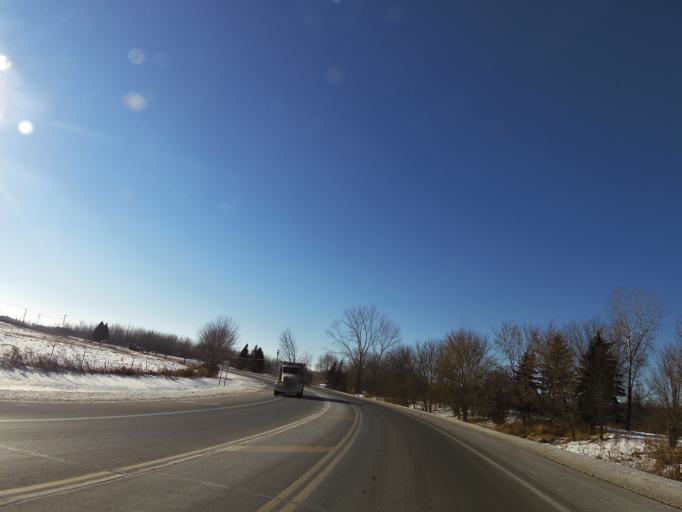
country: US
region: Minnesota
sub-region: Carver County
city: Chaska
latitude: 44.8075
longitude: -93.5714
